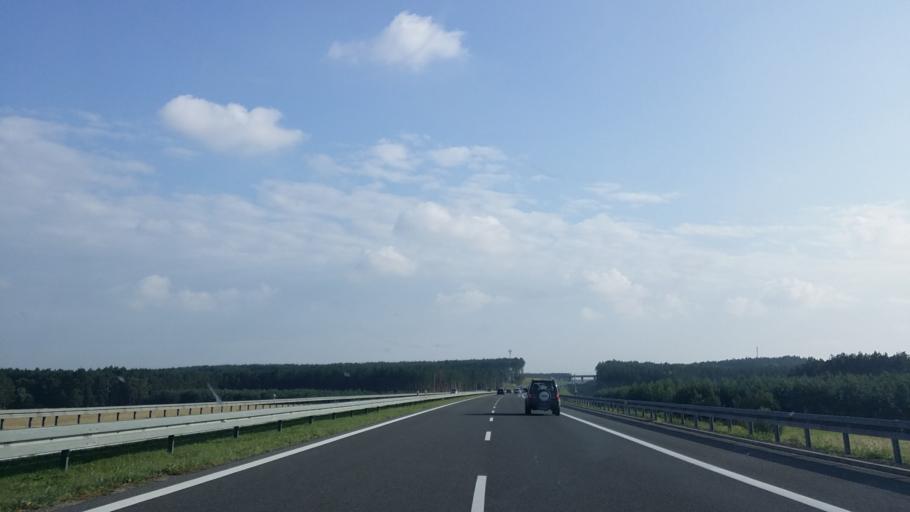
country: PL
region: Lubusz
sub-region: Powiat swiebodzinski
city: Swiebodzin
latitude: 52.3343
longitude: 15.5568
